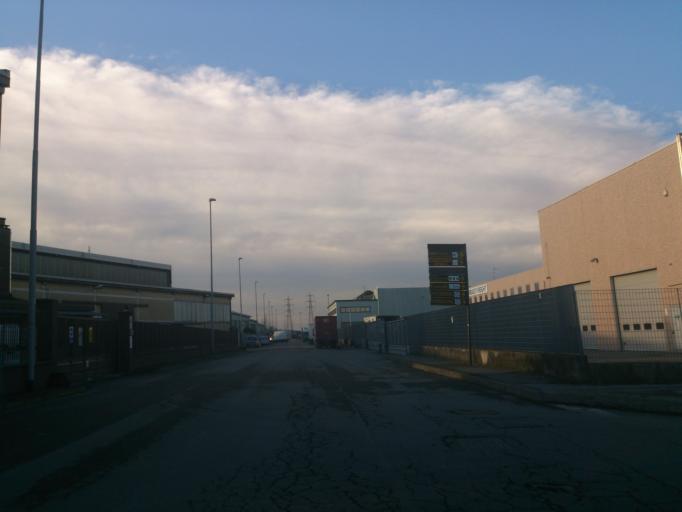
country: IT
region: Lombardy
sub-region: Citta metropolitana di Milano
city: Civesio
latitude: 45.4014
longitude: 9.2538
